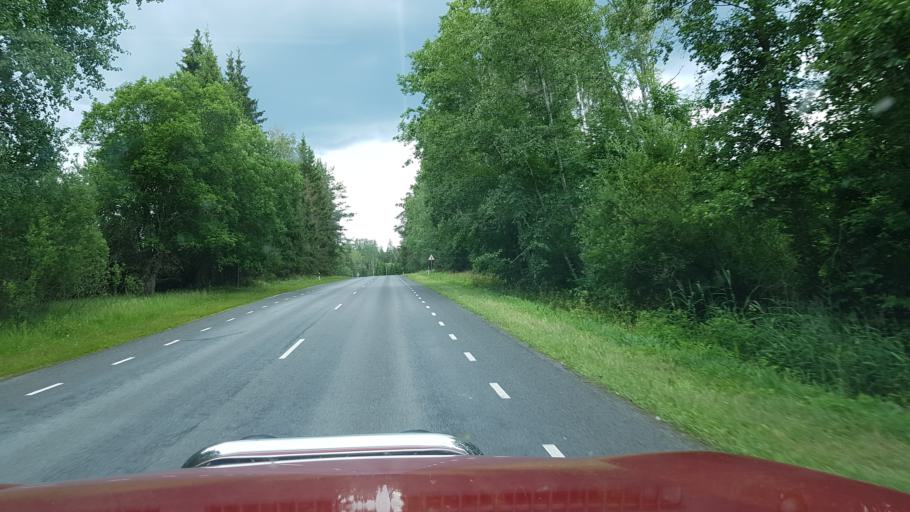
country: EE
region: Polvamaa
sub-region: Polva linn
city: Polva
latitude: 58.1769
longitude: 27.1144
